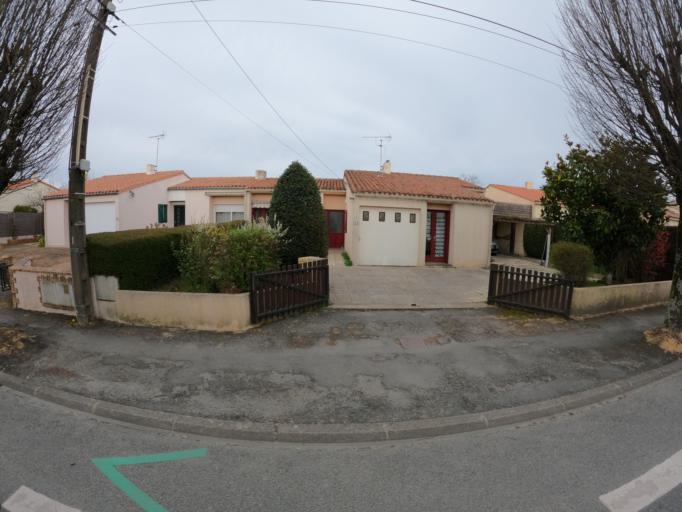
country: FR
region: Pays de la Loire
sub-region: Departement de la Vendee
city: Montaigu
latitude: 46.9827
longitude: -1.3148
